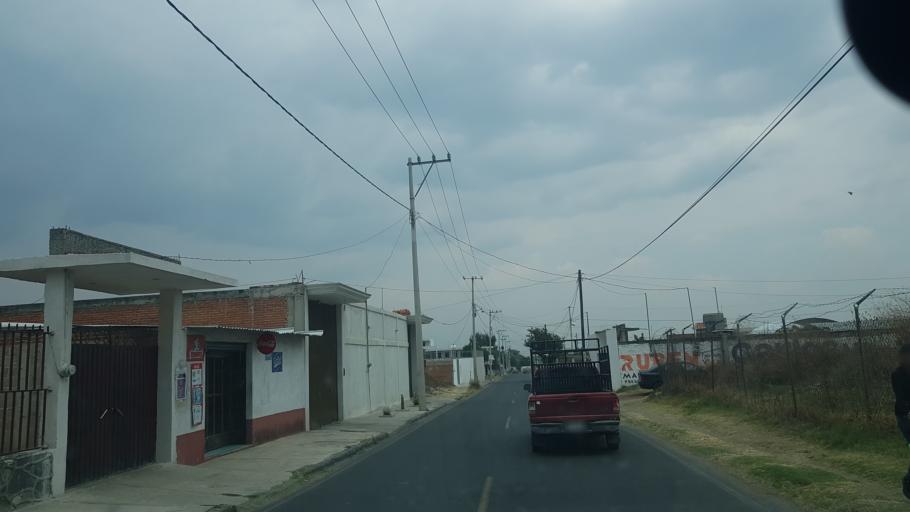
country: MX
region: Puebla
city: San Lorenzo Chiautzingo
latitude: 19.1975
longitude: -98.4437
